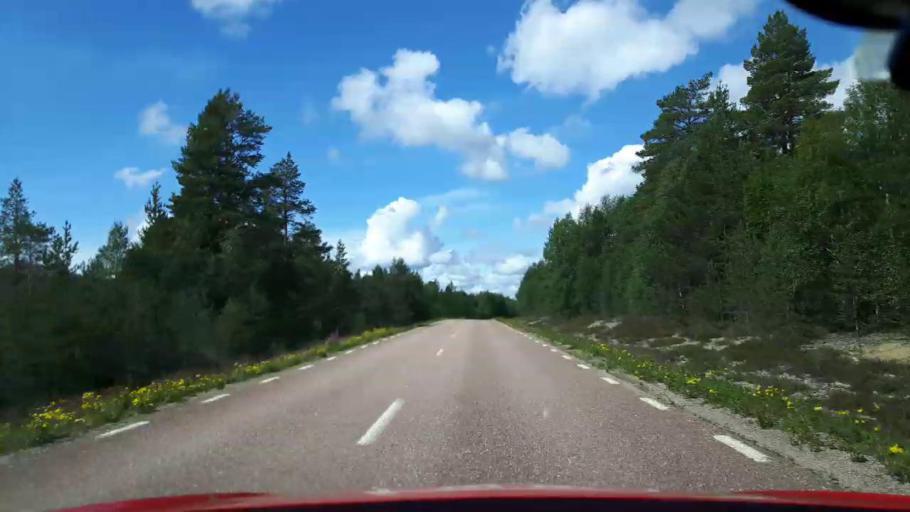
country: SE
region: Dalarna
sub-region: Alvdalens Kommun
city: AElvdalen
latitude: 61.7992
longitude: 13.6749
